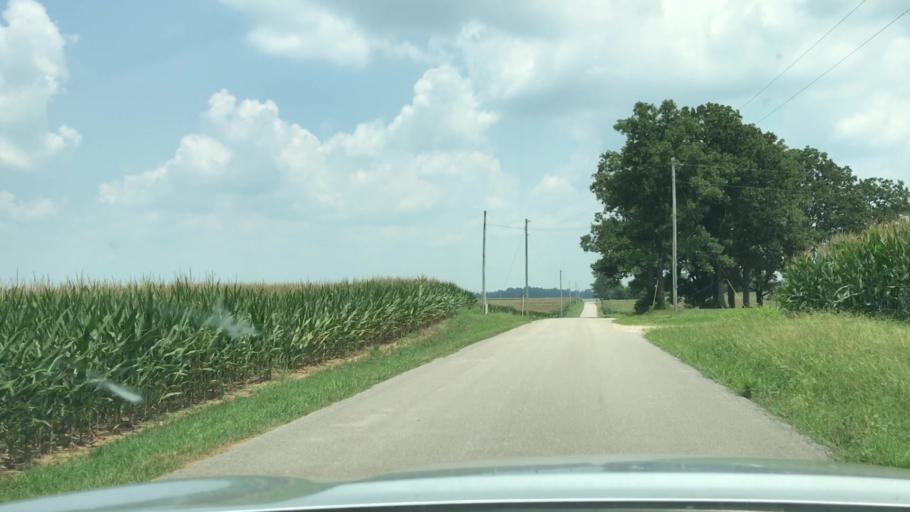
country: US
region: Kentucky
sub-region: Todd County
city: Elkton
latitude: 36.7634
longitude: -87.1182
